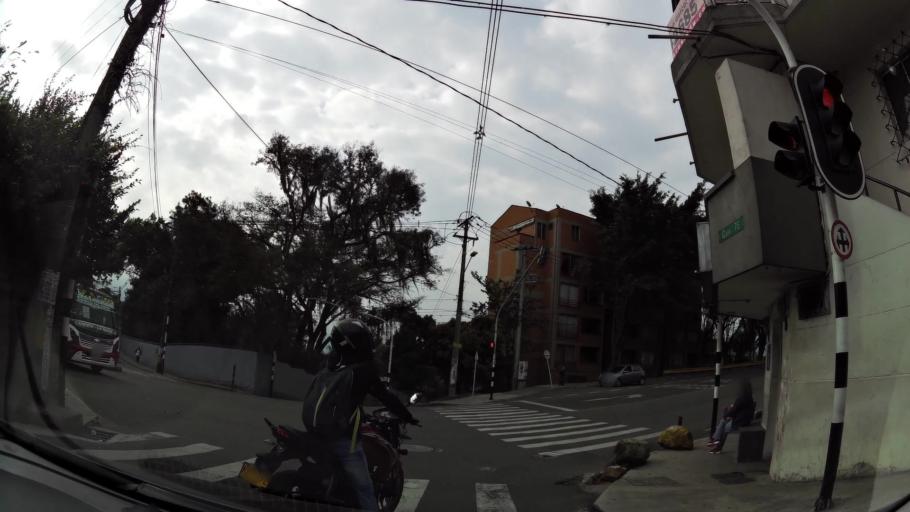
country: CO
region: Antioquia
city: Medellin
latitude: 6.2785
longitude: -75.5933
